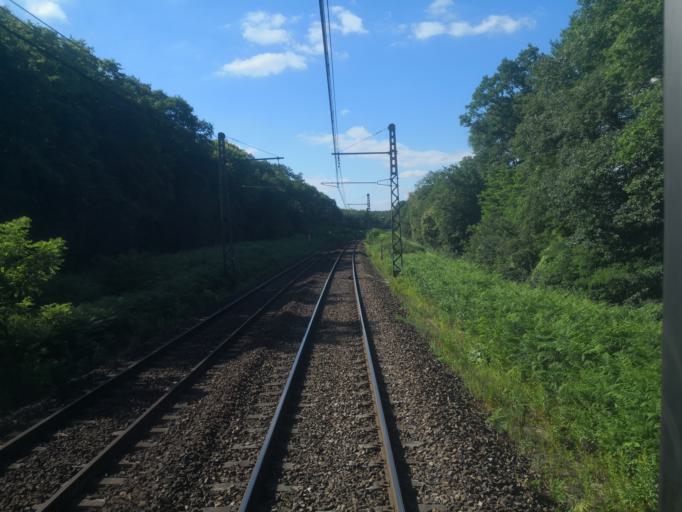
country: FR
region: Ile-de-France
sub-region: Departement de Seine-et-Marne
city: La Rochette
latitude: 48.4882
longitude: 2.6739
